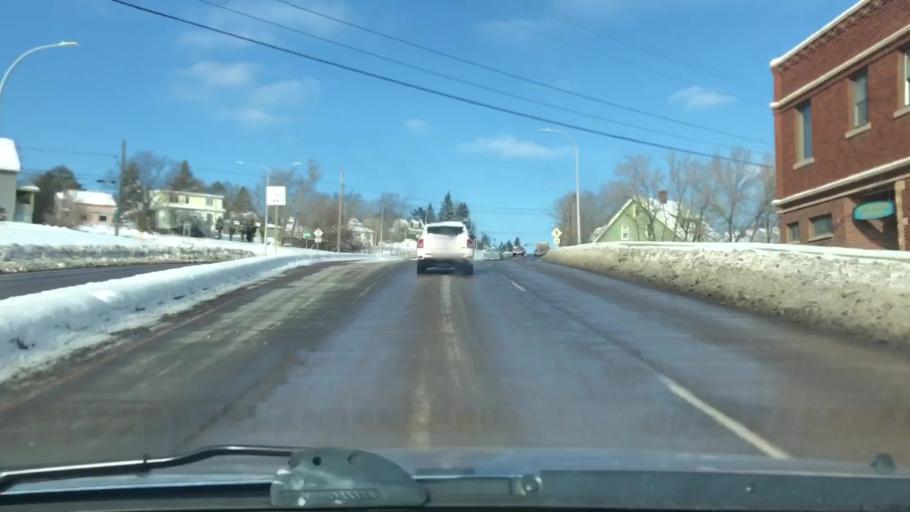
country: US
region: Minnesota
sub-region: Saint Louis County
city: Duluth
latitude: 46.7920
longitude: -92.1070
